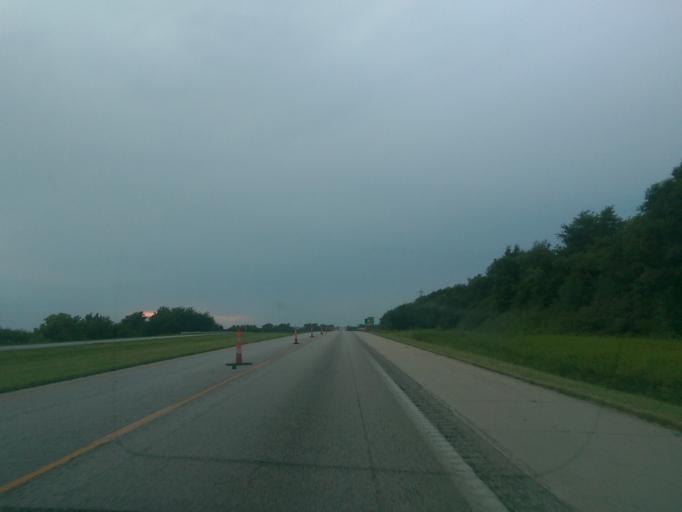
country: US
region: Missouri
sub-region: Holt County
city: Oregon
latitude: 40.0405
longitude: -95.1298
